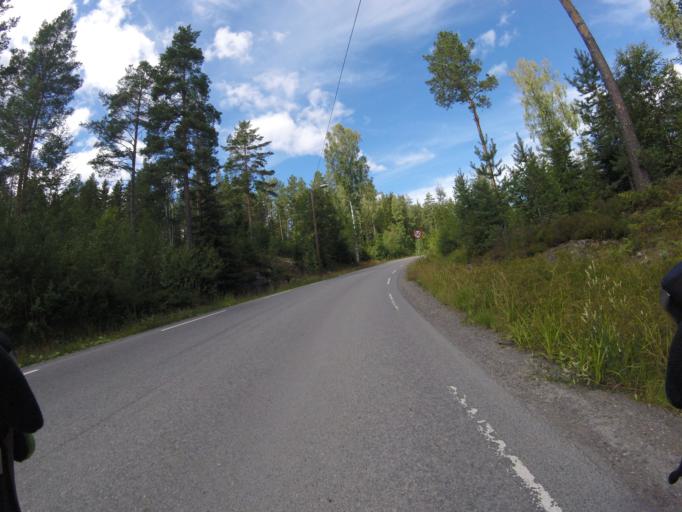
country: NO
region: Akershus
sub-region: Lorenskog
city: Kjenn
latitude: 59.8928
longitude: 10.9758
